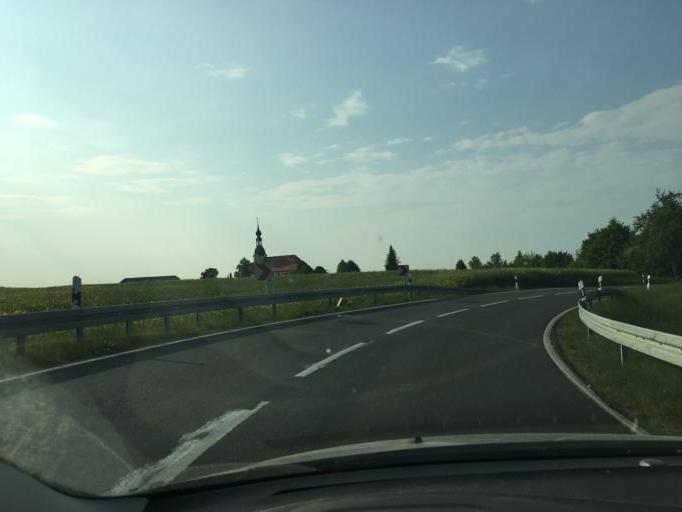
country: DE
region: Saxony
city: Grossbothen
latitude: 51.1482
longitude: 12.7649
